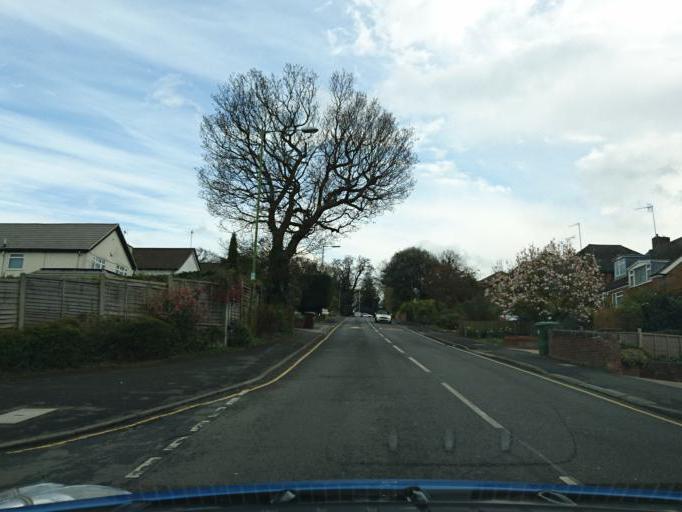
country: GB
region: England
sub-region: Hertfordshire
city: Borehamwood
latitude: 51.6462
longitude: -0.2802
